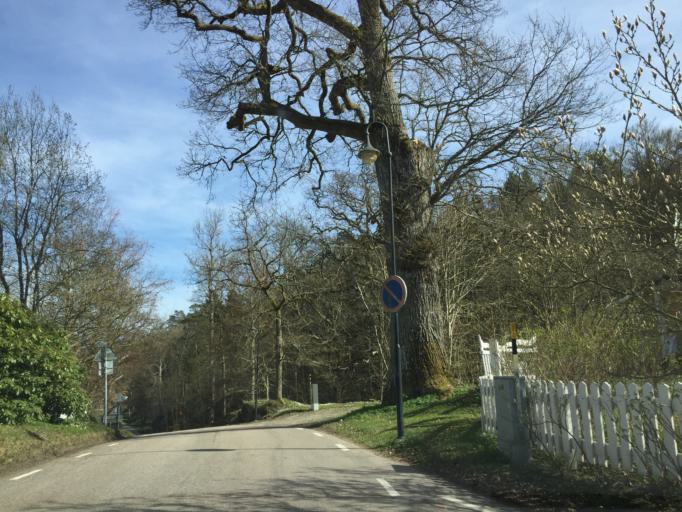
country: SE
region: Vaestra Goetaland
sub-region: Uddevalla Kommun
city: Uddevalla
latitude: 58.3283
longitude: 11.9066
